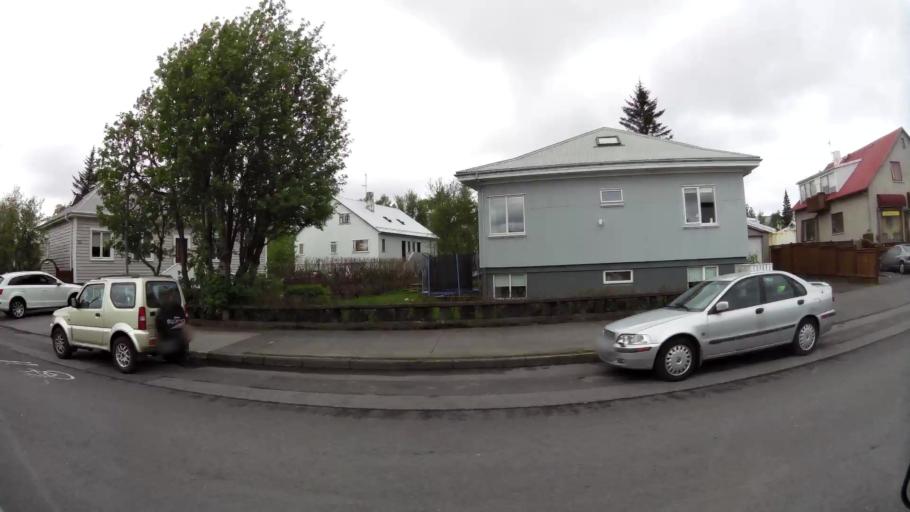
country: IS
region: Capital Region
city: Reykjavik
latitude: 64.1301
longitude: -21.8528
